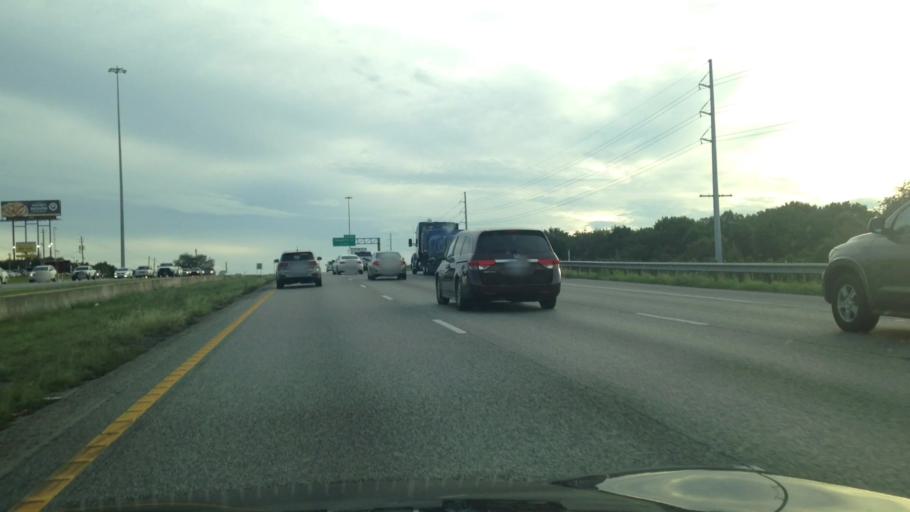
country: US
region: Texas
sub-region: Travis County
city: Onion Creek
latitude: 30.1773
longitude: -97.7795
